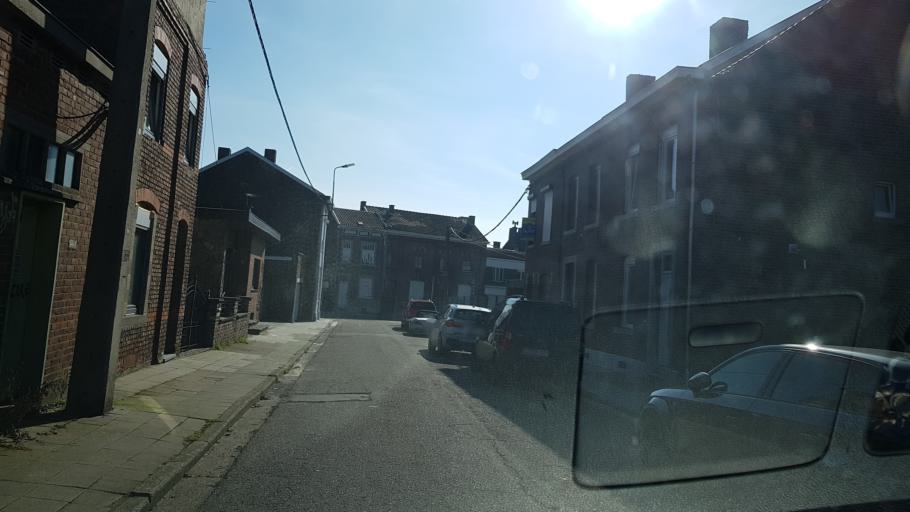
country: BE
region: Wallonia
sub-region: Province de Liege
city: Oupeye
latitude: 50.6973
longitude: 5.6534
